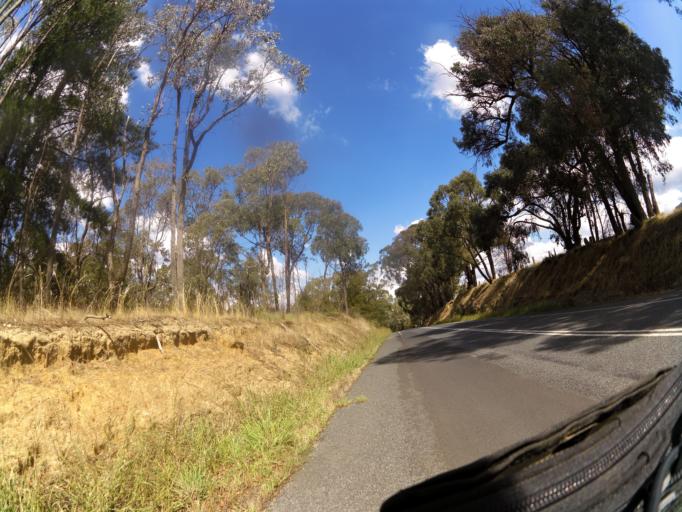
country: AU
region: Victoria
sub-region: Mansfield
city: Mansfield
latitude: -36.8196
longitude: 146.0075
